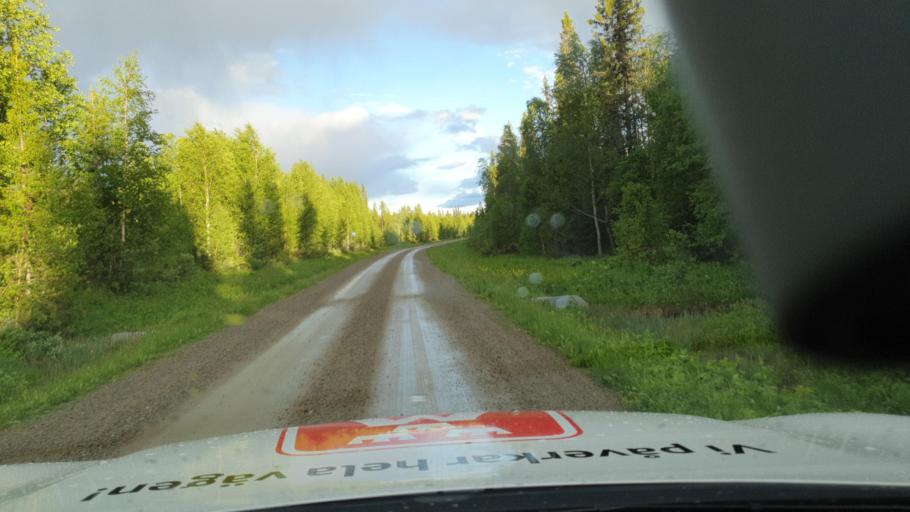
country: SE
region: Vaesterbotten
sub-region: Storumans Kommun
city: Storuman
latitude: 64.7546
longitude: 17.0815
